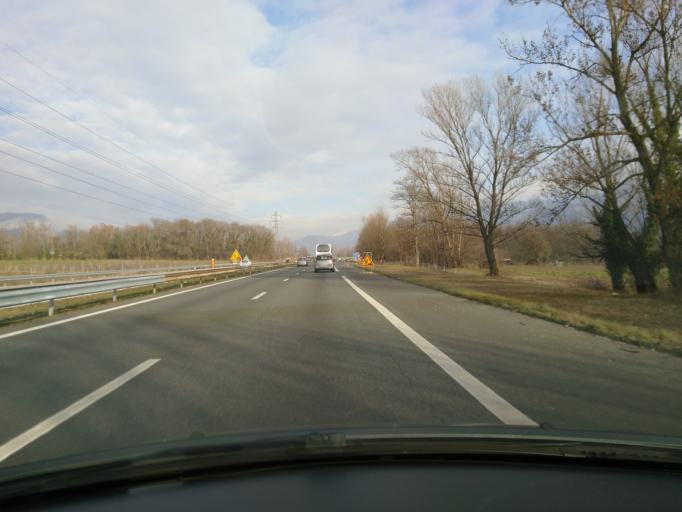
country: FR
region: Rhone-Alpes
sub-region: Departement de l'Isere
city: Saint-Ismier
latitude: 45.2368
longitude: 5.8399
